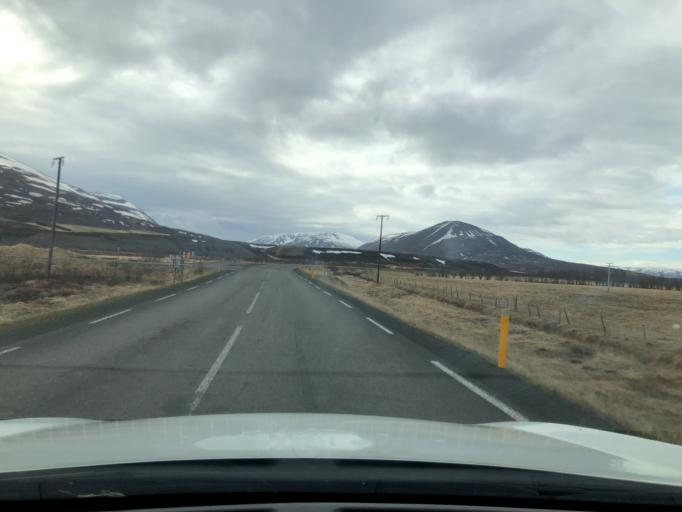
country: IS
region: Northeast
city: Akureyri
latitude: 65.7746
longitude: -17.9164
